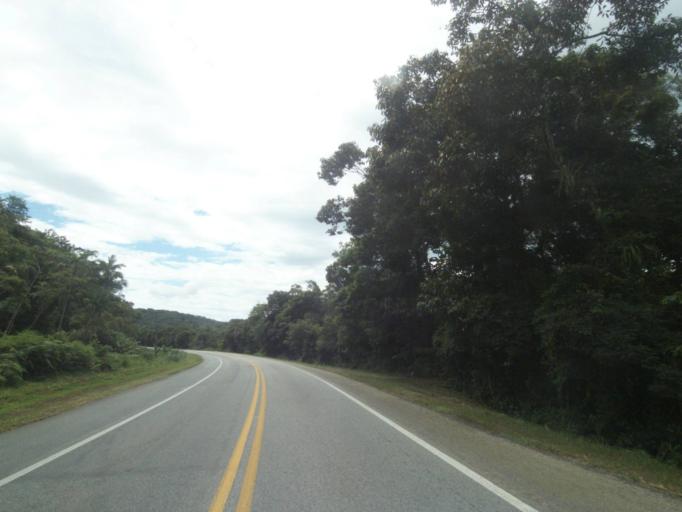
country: BR
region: Parana
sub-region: Antonina
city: Antonina
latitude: -25.4488
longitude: -48.7766
